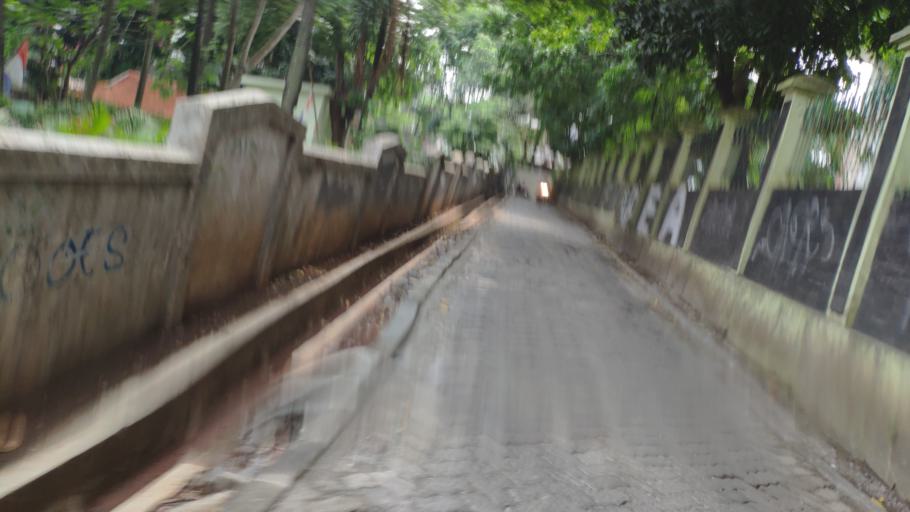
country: ID
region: Jakarta Raya
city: Jakarta
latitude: -6.3032
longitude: 106.8261
